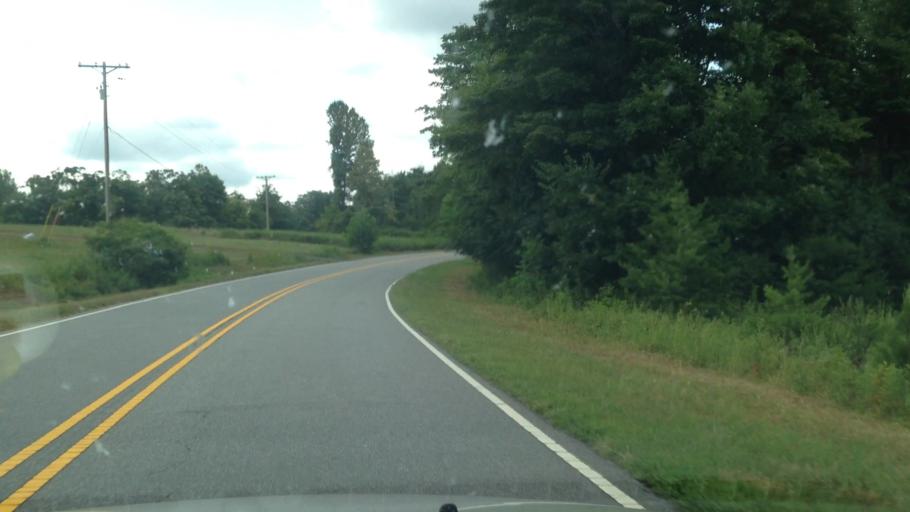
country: US
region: North Carolina
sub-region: Rockingham County
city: Mayodan
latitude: 36.4190
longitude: -80.0687
